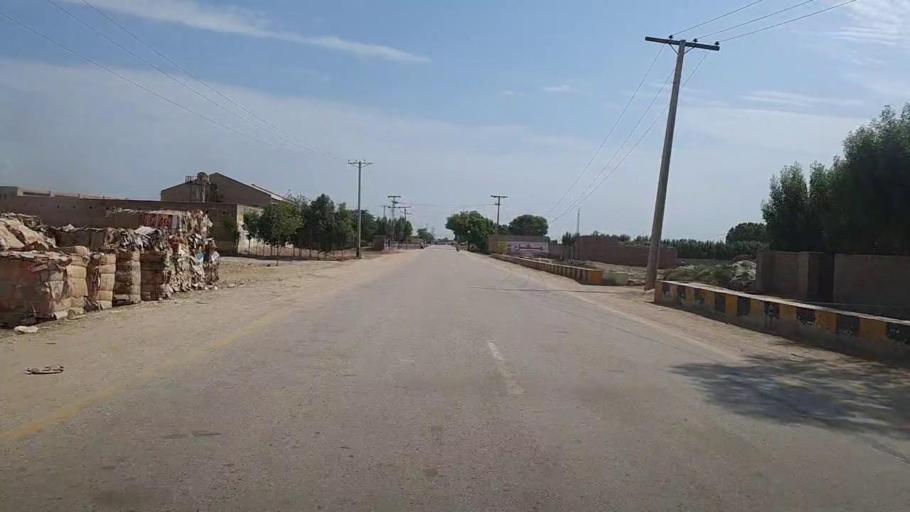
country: PK
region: Sindh
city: Thul
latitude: 28.2359
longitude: 68.7900
